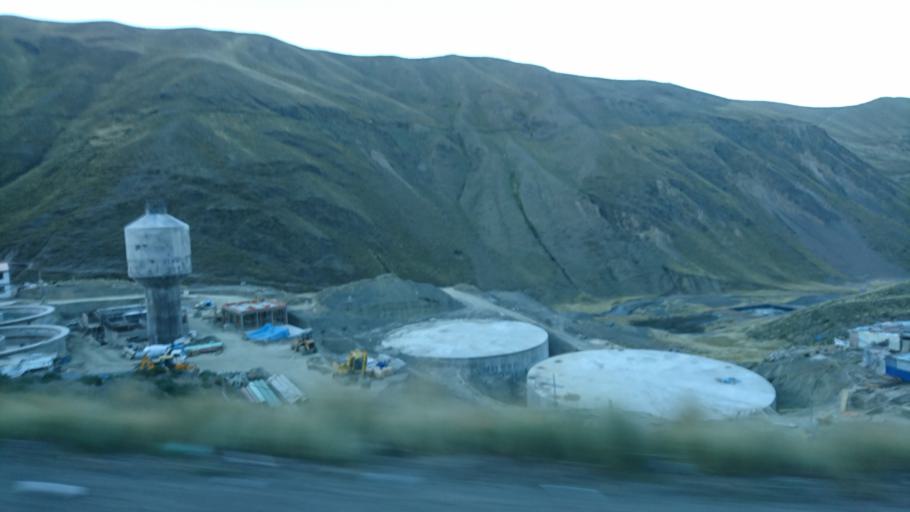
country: BO
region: La Paz
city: La Paz
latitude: -16.4219
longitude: -68.0570
